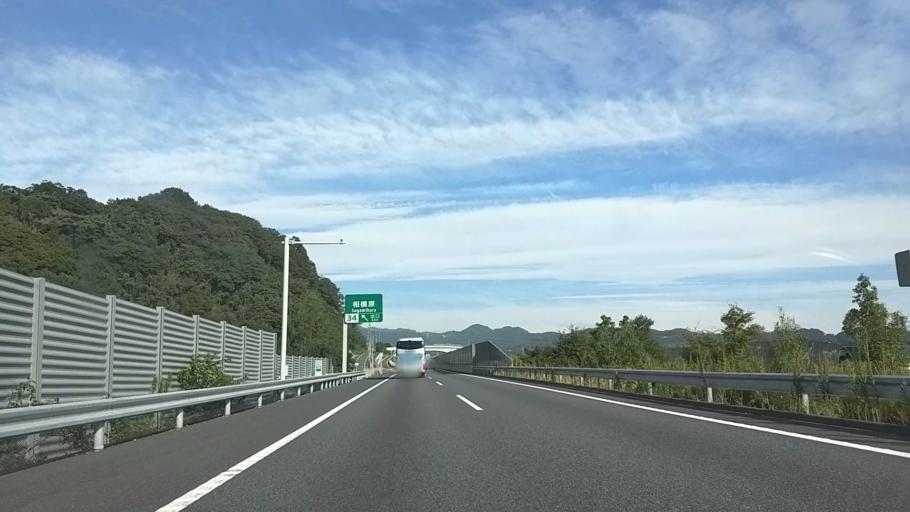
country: JP
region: Tokyo
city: Hachioji
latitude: 35.5770
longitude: 139.2975
